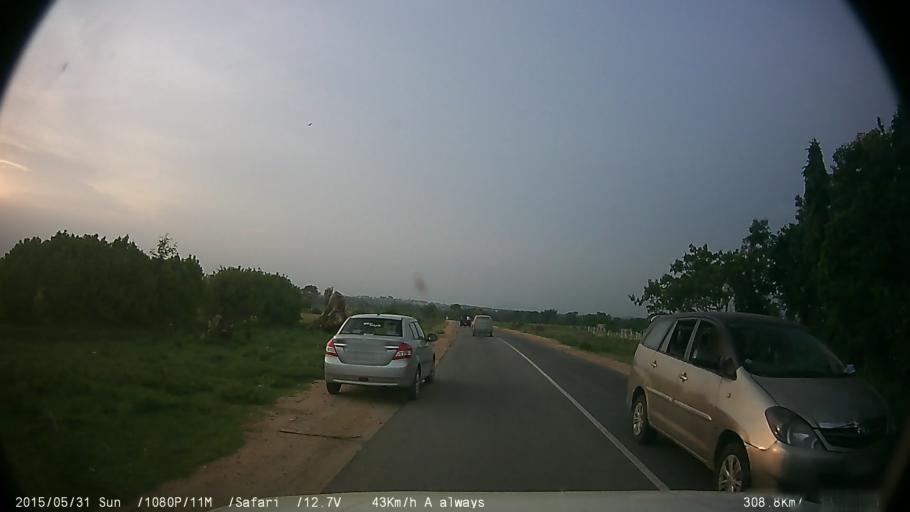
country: IN
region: Karnataka
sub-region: Mysore
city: Nanjangud
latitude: 12.0825
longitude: 76.6752
